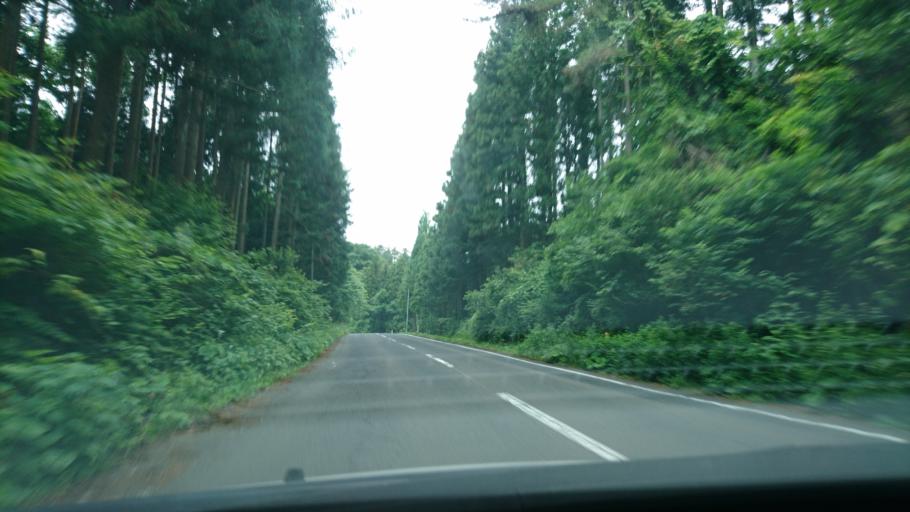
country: JP
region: Iwate
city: Ichinoseki
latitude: 38.9452
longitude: 141.2768
